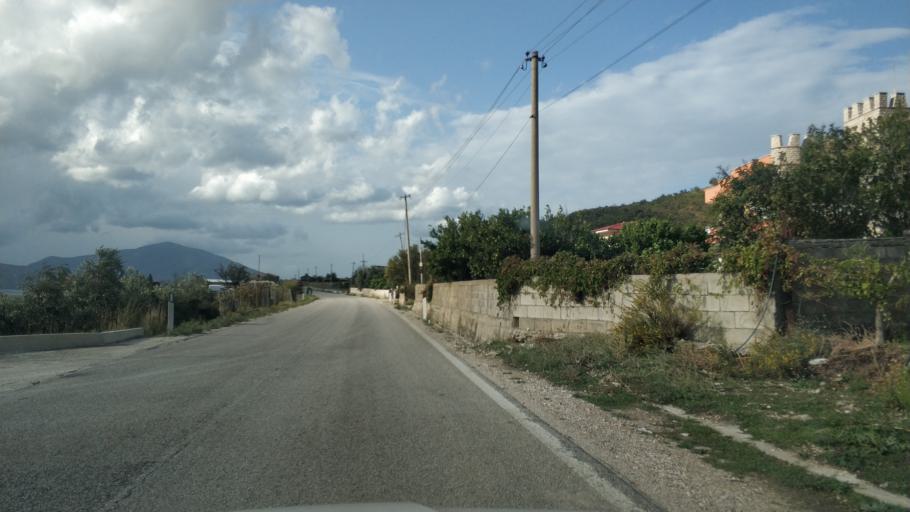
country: AL
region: Vlore
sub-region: Rrethi i Vlores
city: Orikum
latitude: 40.2961
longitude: 19.4899
